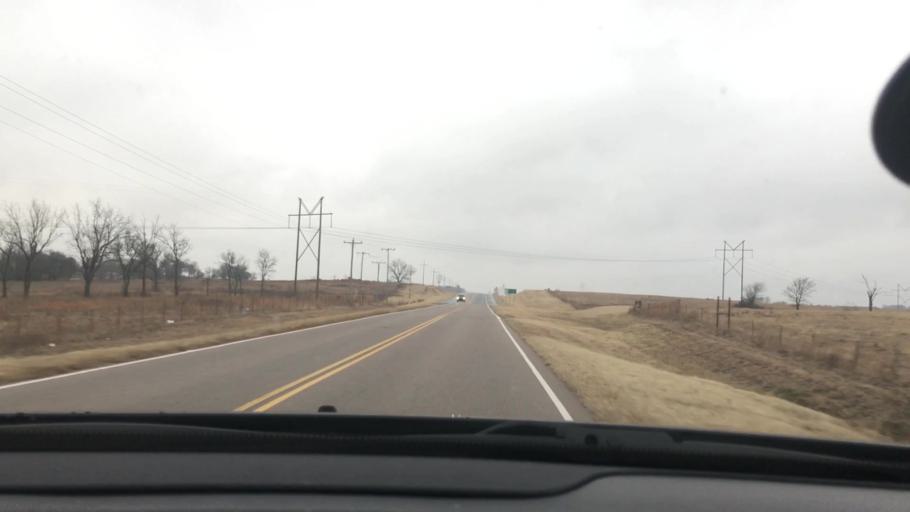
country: US
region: Oklahoma
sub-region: Johnston County
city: Tishomingo
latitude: 34.3689
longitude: -96.6360
